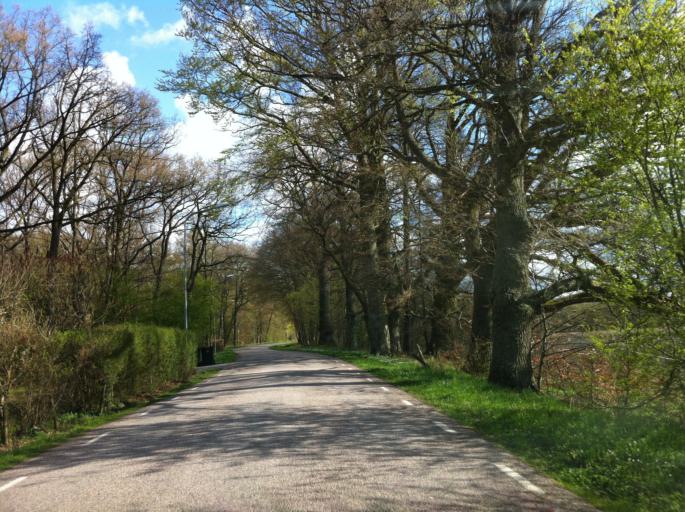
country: SE
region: Skane
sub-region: Eslovs Kommun
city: Stehag
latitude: 55.9066
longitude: 13.4319
